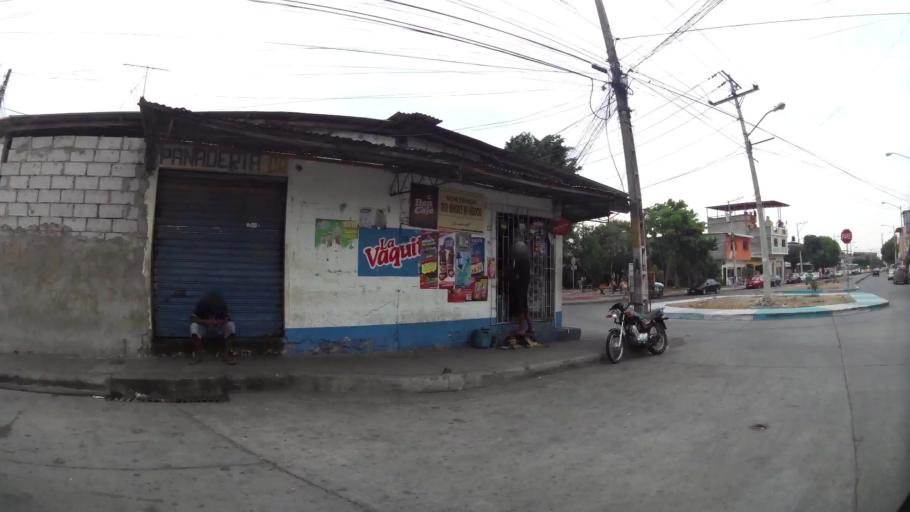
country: EC
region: Guayas
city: Guayaquil
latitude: -2.2576
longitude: -79.8849
